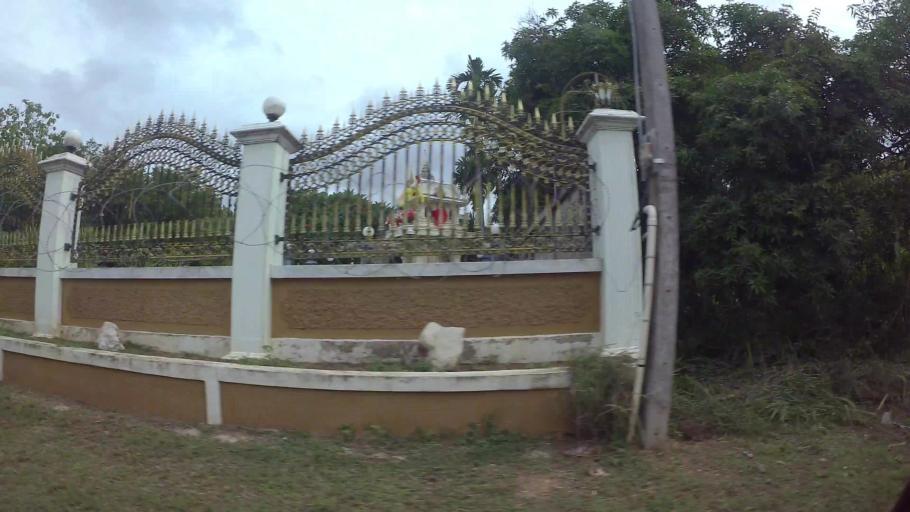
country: TH
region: Chon Buri
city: Sattahip
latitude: 12.7188
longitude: 100.9108
